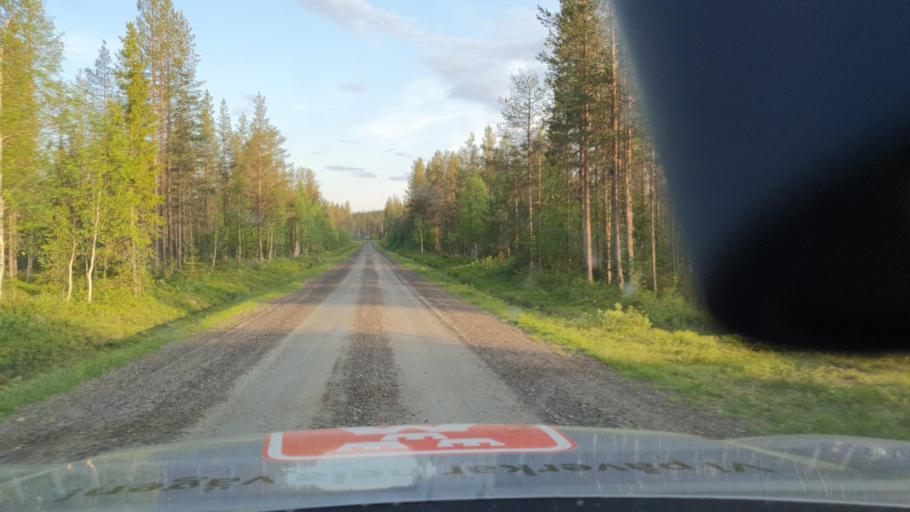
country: SE
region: Norrbotten
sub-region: Bodens Kommun
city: Boden
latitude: 66.4247
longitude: 21.7149
